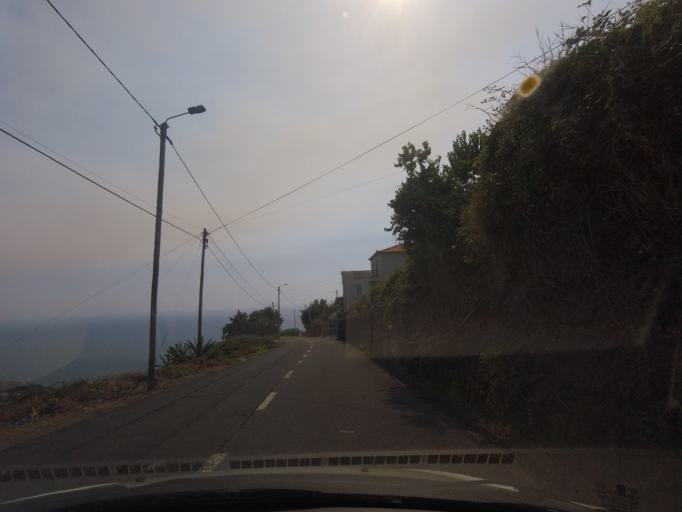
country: PT
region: Madeira
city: Ribeira Brava
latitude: 32.6828
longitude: -17.0673
